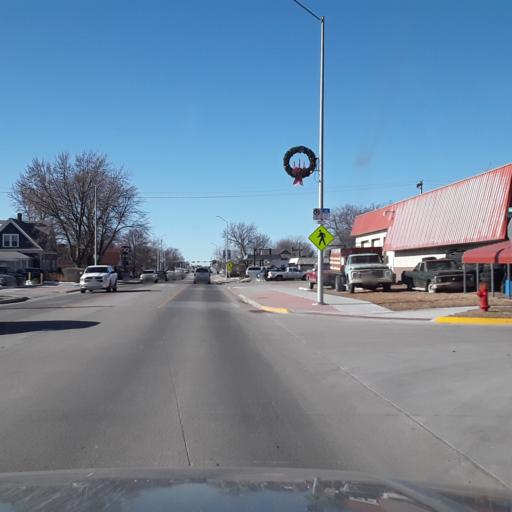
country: US
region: Nebraska
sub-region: Phelps County
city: Holdrege
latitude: 40.4380
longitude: -99.3749
